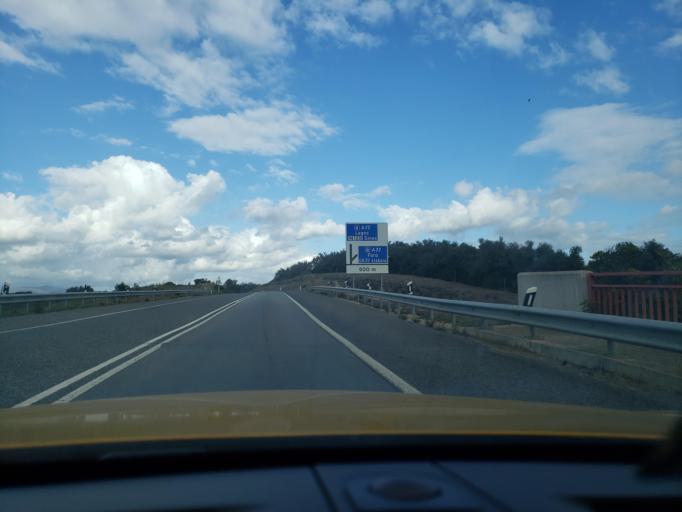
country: PT
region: Faro
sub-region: Portimao
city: Portimao
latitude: 37.1682
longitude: -8.5691
